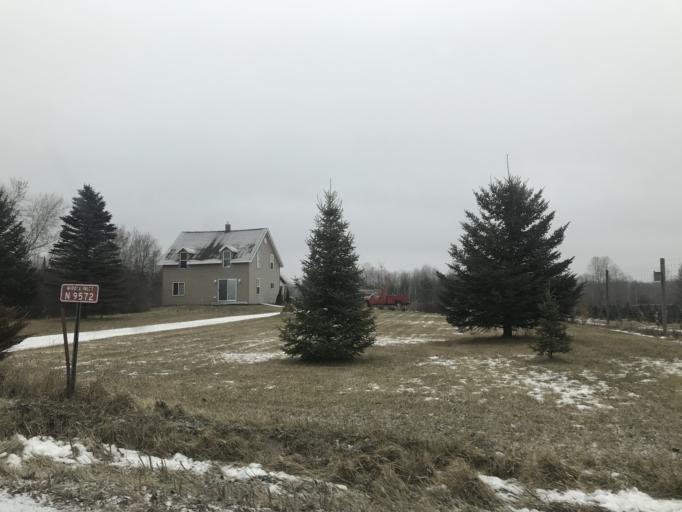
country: US
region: Wisconsin
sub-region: Marinette County
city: Peshtigo
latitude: 45.3017
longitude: -87.8678
